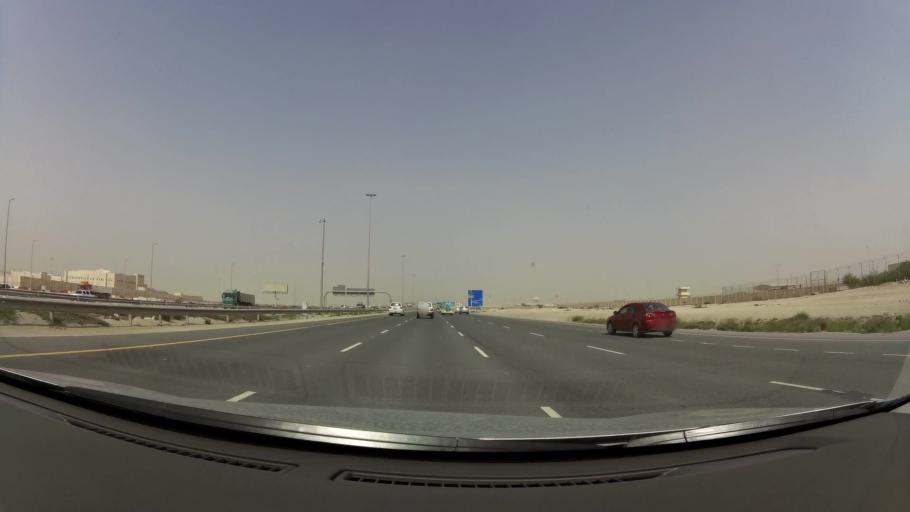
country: QA
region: Baladiyat ar Rayyan
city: Ar Rayyan
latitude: 25.2036
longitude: 51.3942
